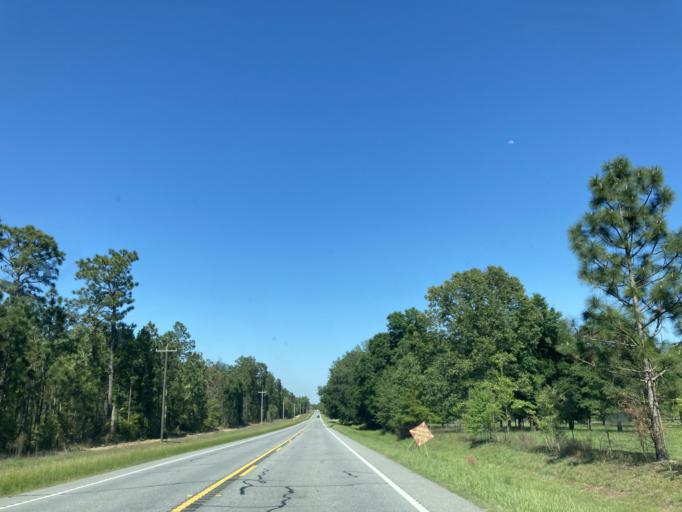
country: US
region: Georgia
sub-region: Baker County
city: Newton
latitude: 31.2828
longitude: -84.3693
